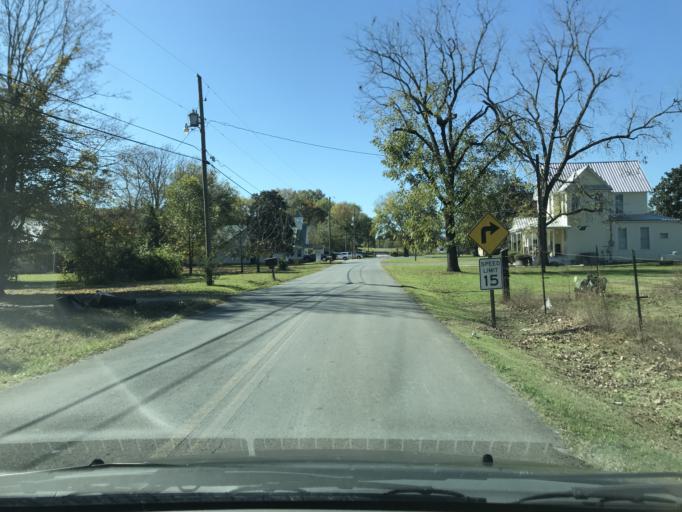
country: US
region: Georgia
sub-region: Dade County
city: Trenton
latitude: 34.9095
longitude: -85.4769
